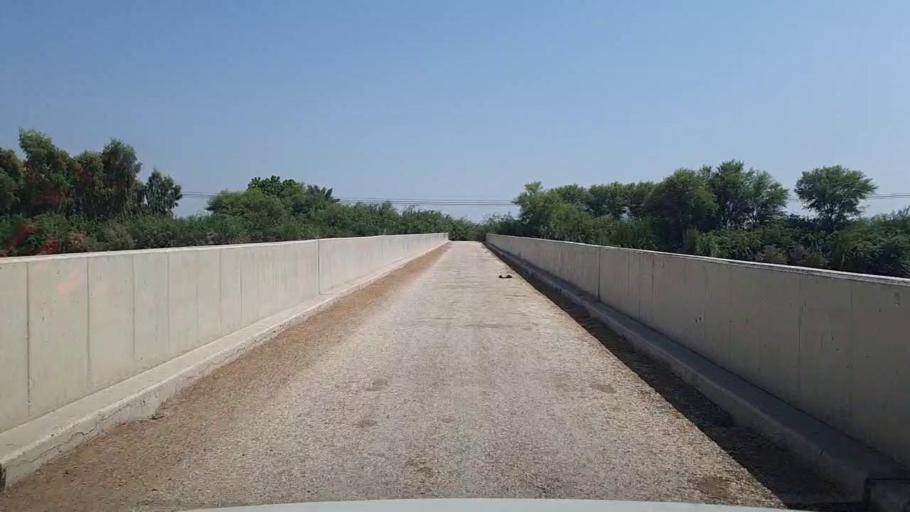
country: PK
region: Sindh
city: Kandhkot
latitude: 28.2878
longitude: 69.3538
